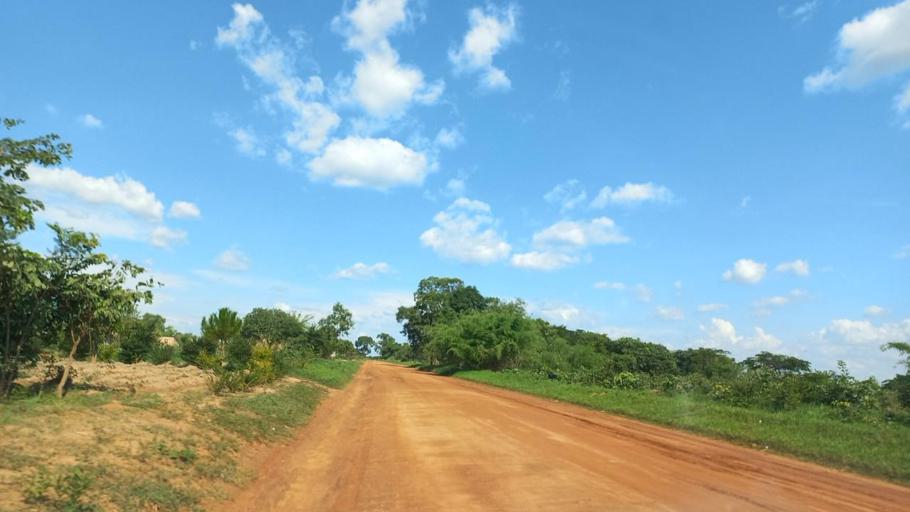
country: ZM
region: Copperbelt
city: Kitwe
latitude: -12.8703
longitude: 28.3508
